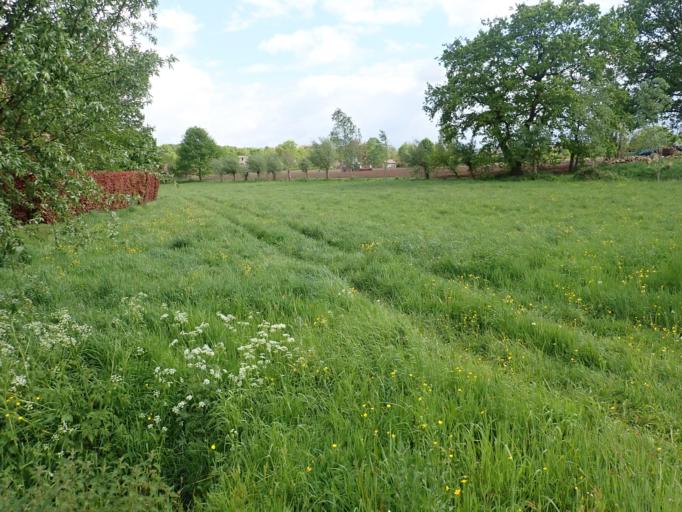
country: BE
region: Flanders
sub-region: Provincie Antwerpen
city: Puurs
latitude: 51.0671
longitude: 4.2761
